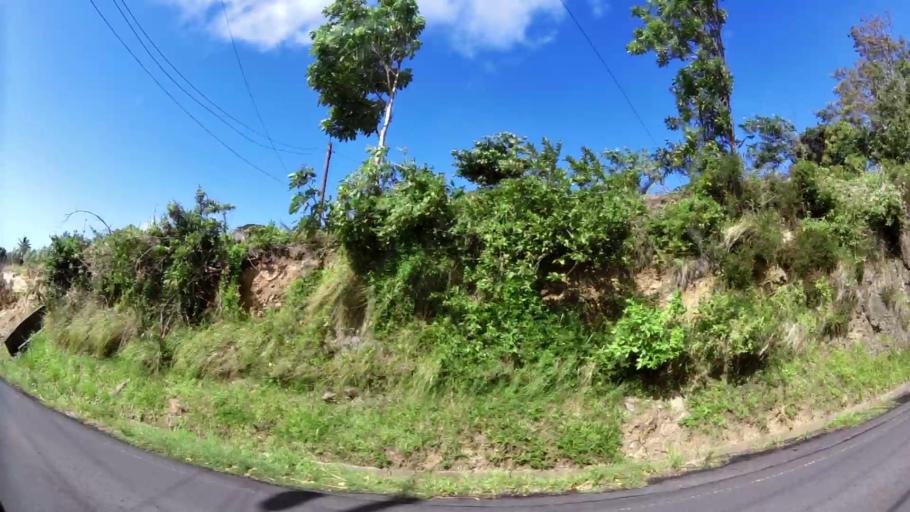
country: LC
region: Choiseul Quarter
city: Choiseul
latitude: 13.8018
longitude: -61.0367
